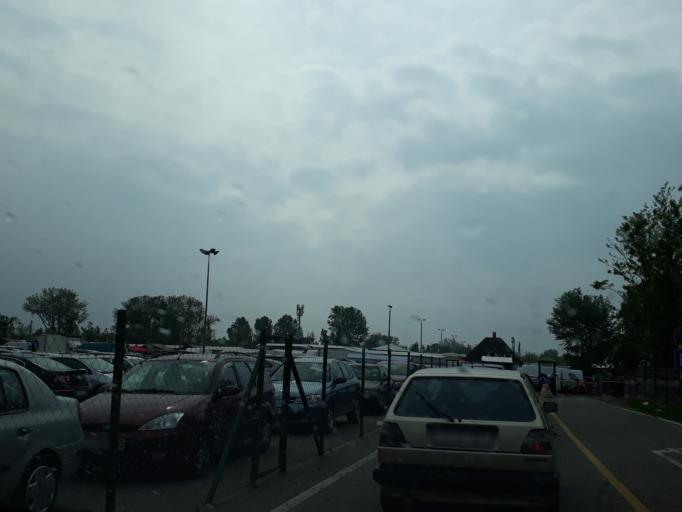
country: HU
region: Szabolcs-Szatmar-Bereg
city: Nyiregyhaza
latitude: 47.9689
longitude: 21.6918
